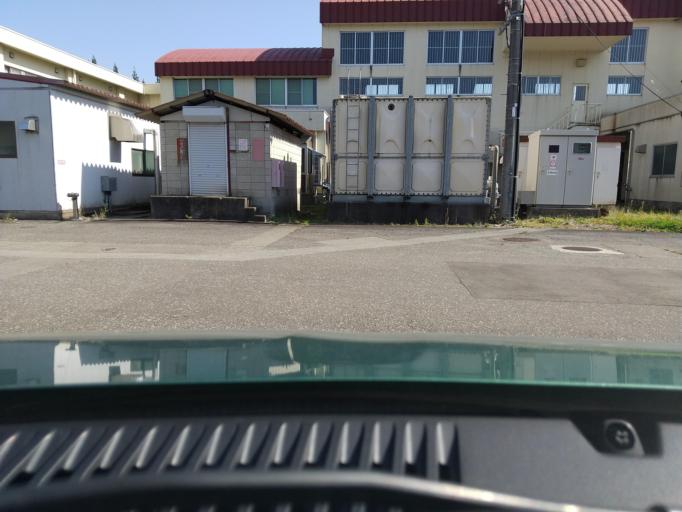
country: JP
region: Akita
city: Akita
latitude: 39.5974
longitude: 140.3018
